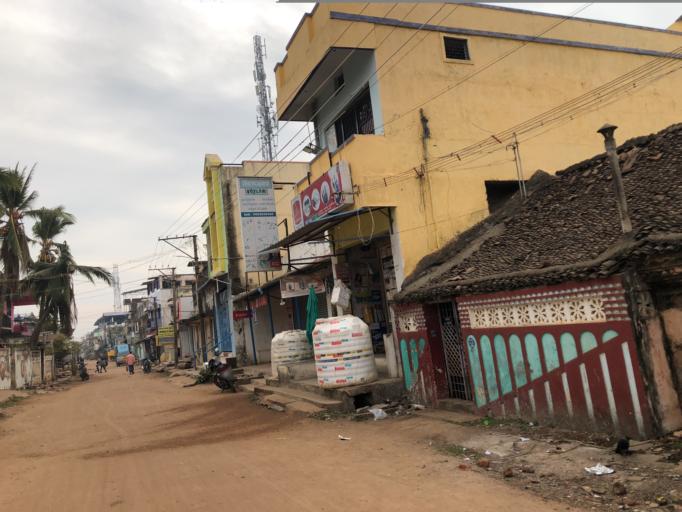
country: IN
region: Tamil Nadu
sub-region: Thanjavur
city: Adirampattinam
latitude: 10.3400
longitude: 79.3820
